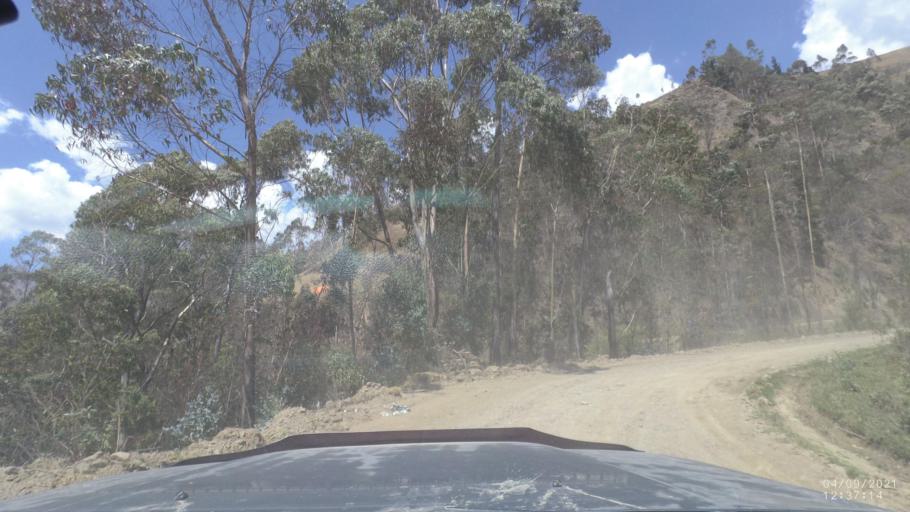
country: BO
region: Cochabamba
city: Colchani
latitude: -17.2265
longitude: -66.5043
